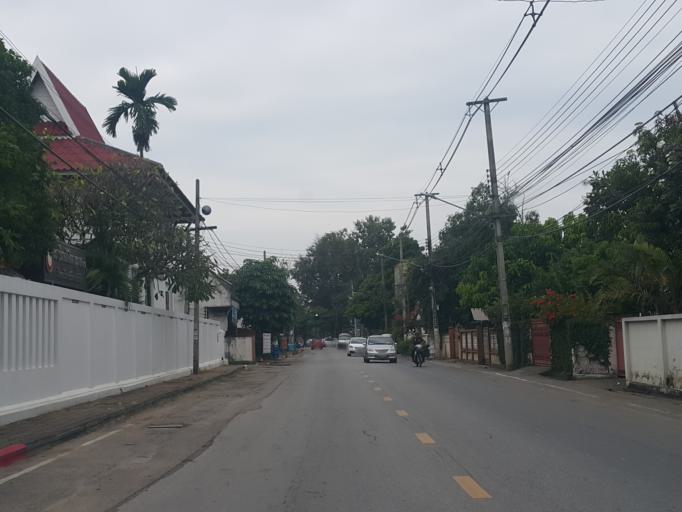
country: TH
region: Lampang
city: Lampang
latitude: 18.2920
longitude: 99.5067
